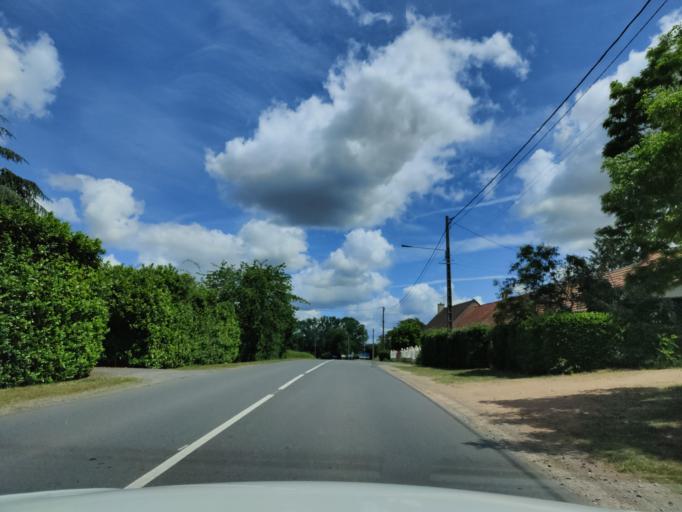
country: FR
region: Auvergne
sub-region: Departement de l'Allier
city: Estivareilles
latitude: 46.4582
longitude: 2.6141
